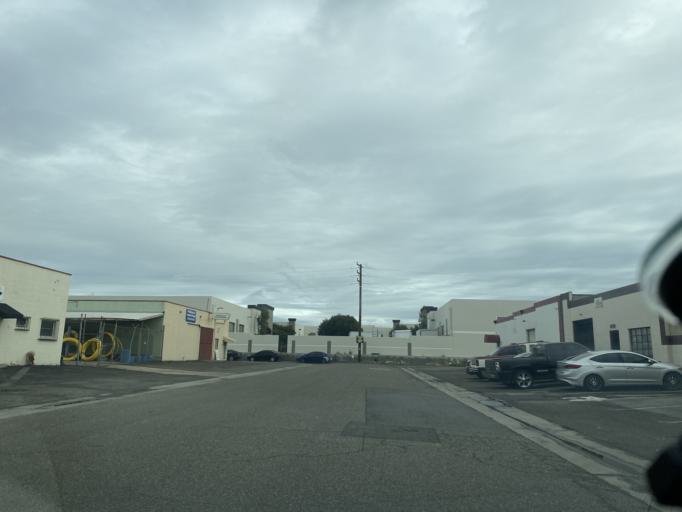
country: US
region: California
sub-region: Orange County
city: Fullerton
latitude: 33.8656
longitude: -117.9055
